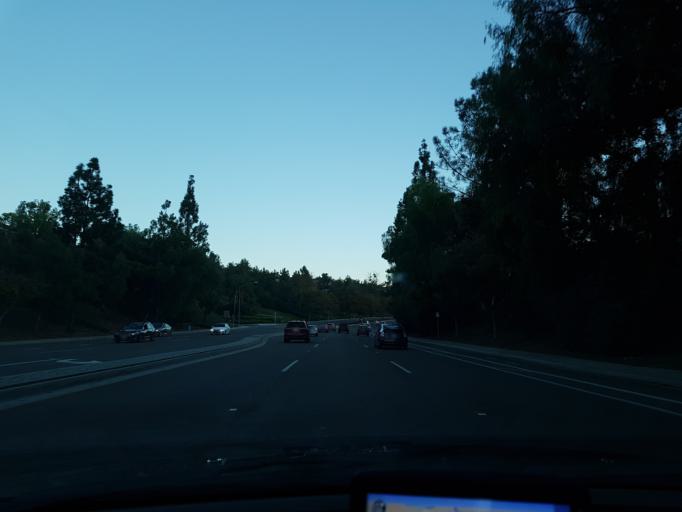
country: US
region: California
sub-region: San Diego County
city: Fairbanks Ranch
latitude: 32.9368
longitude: -117.1269
